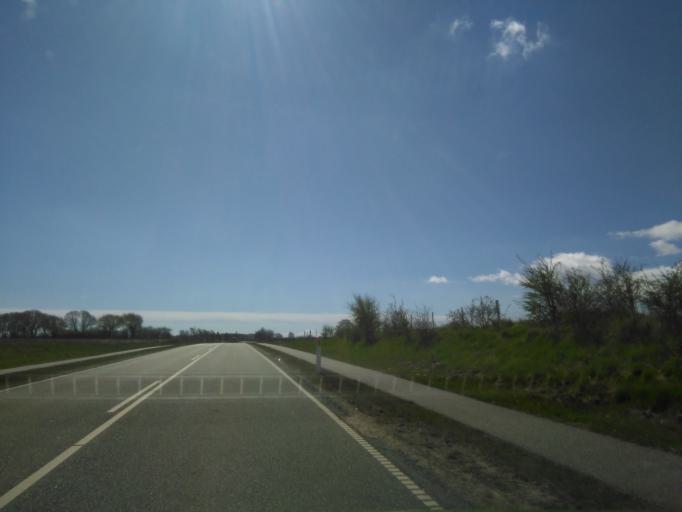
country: DK
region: Central Jutland
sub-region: Hedensted Kommune
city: Juelsminde
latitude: 55.7979
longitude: 10.0091
